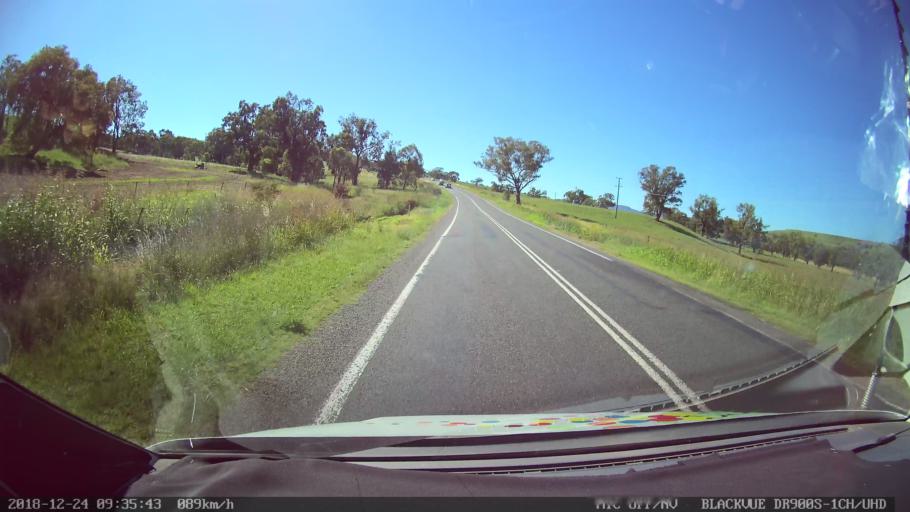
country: AU
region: New South Wales
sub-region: Liverpool Plains
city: Quirindi
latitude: -31.6329
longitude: 150.7192
